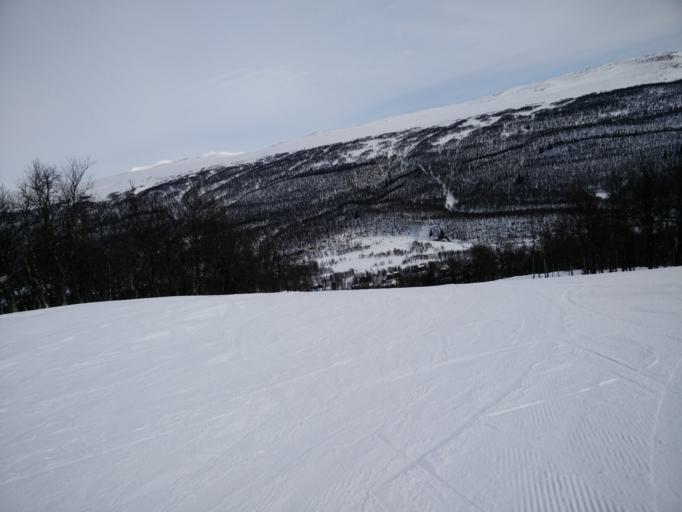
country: NO
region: Sor-Trondelag
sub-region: Tydal
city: Aas
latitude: 62.7021
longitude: 12.3727
